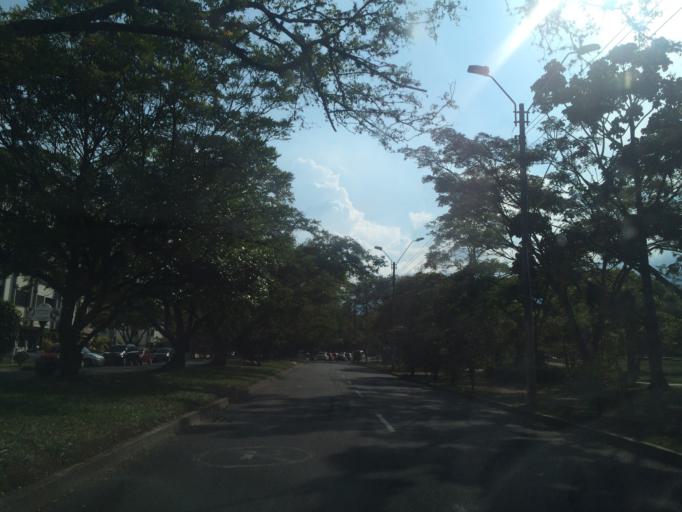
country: CO
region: Valle del Cauca
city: Cali
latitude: 3.3831
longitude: -76.5368
